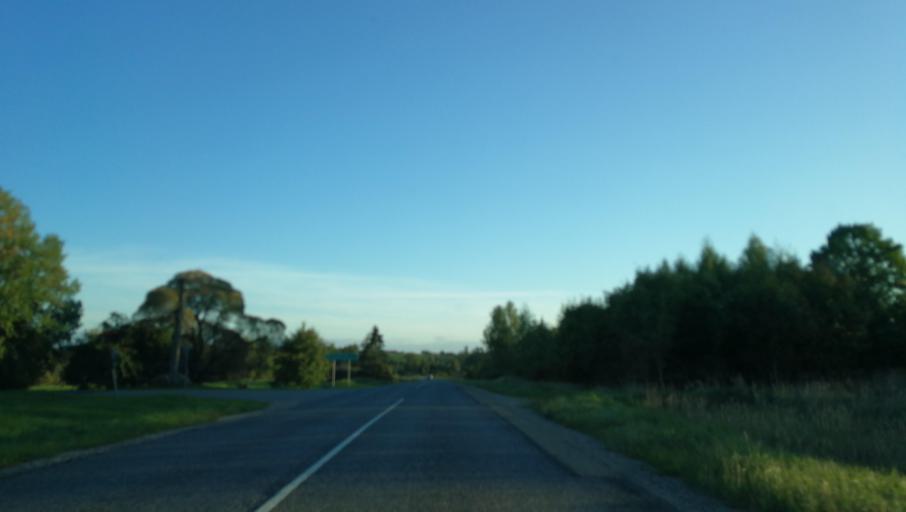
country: LV
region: Aizpute
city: Aizpute
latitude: 56.6746
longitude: 21.6399
